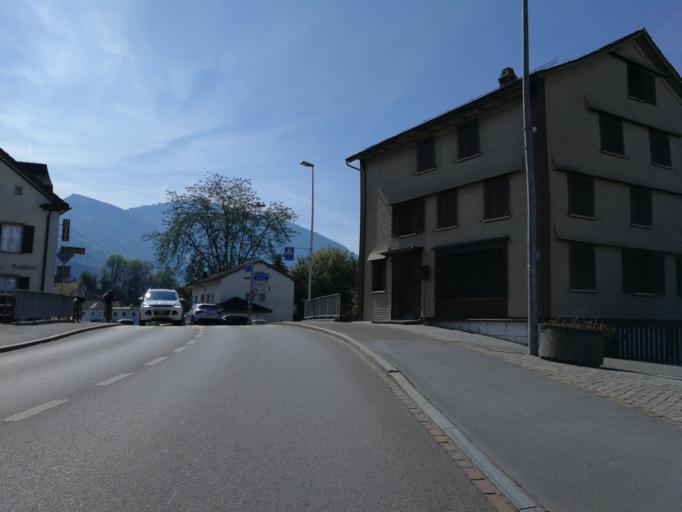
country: CH
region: Saint Gallen
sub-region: Wahlkreis See-Gaster
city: Kaltbrunn
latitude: 47.2131
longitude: 9.0252
